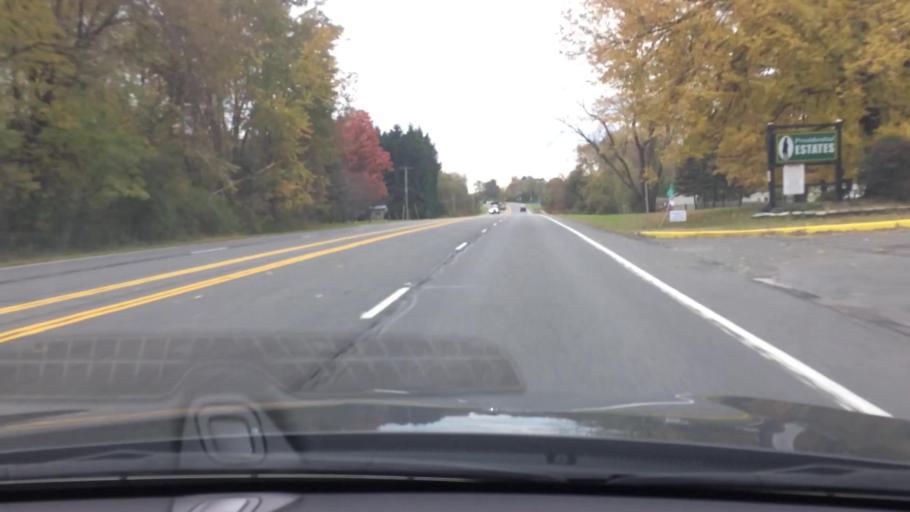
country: US
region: New York
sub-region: Columbia County
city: Kinderhook
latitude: 42.3962
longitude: -73.6870
